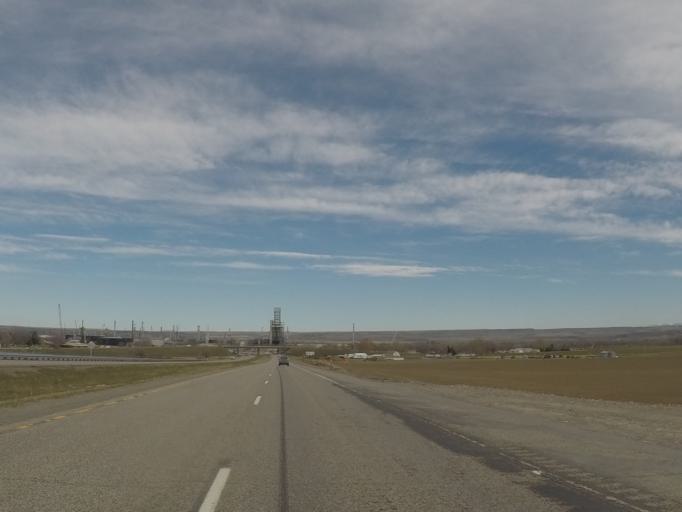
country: US
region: Montana
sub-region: Yellowstone County
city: Laurel
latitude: 45.6632
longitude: -108.7882
